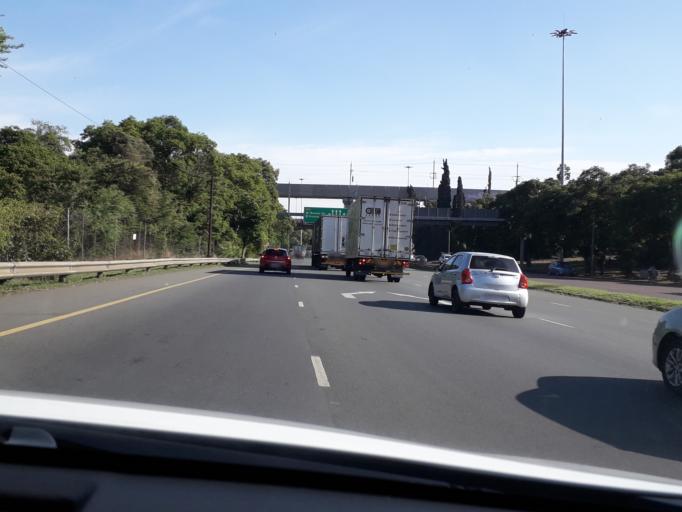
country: ZA
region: Gauteng
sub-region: City of Tshwane Metropolitan Municipality
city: Pretoria
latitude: -25.7659
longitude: 28.1949
